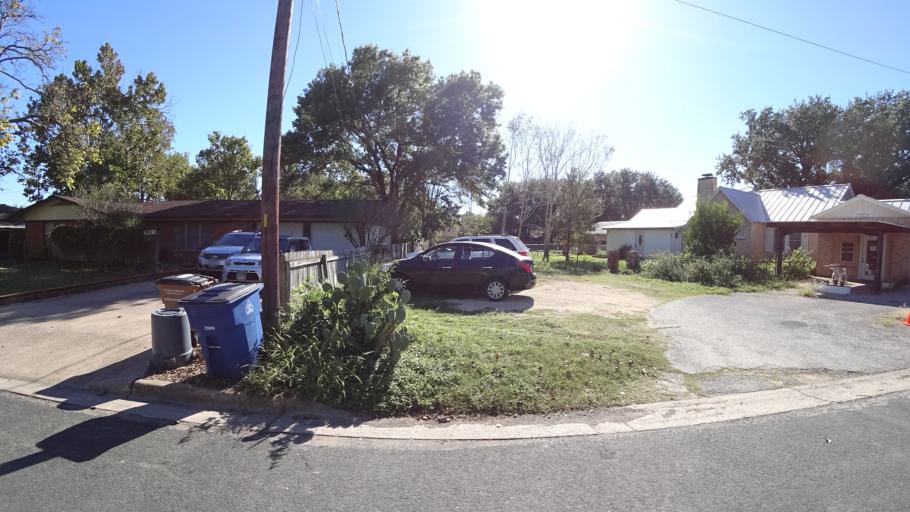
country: US
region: Texas
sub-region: Travis County
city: Rollingwood
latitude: 30.2332
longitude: -97.7870
